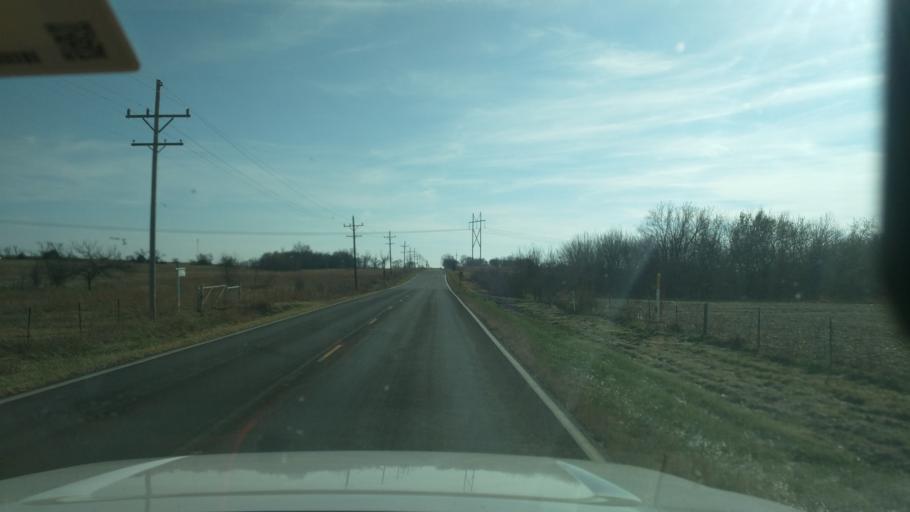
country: US
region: Kansas
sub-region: Lyon County
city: Emporia
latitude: 38.2926
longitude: -96.1805
